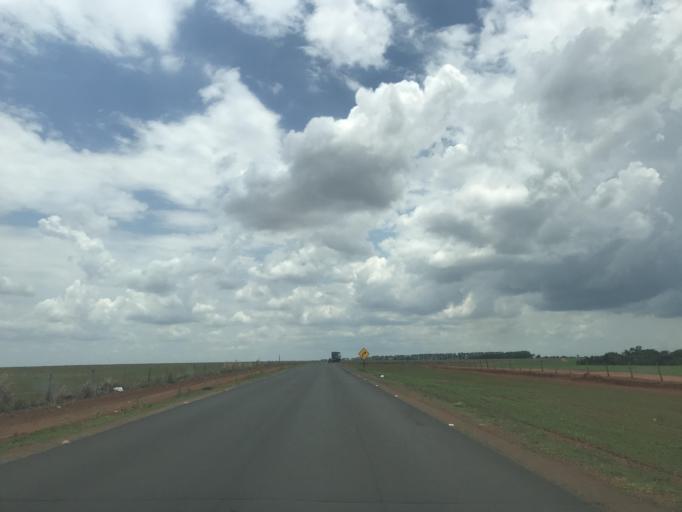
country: BR
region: Goias
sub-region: Vianopolis
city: Vianopolis
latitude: -16.7768
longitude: -48.5221
